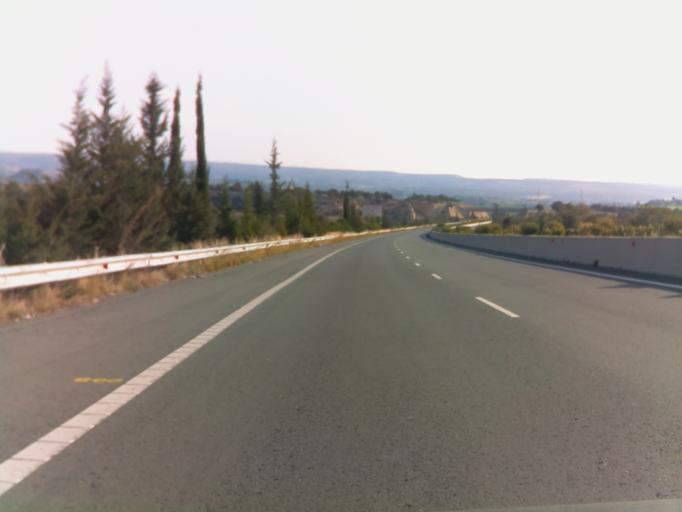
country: CY
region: Limassol
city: Pissouri
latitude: 34.6846
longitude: 32.7324
